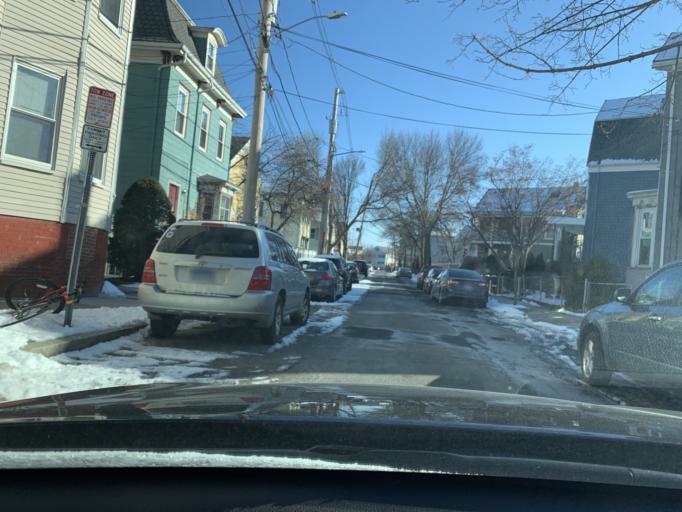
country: US
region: Massachusetts
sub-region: Middlesex County
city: Cambridge
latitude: 42.3758
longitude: -71.0987
